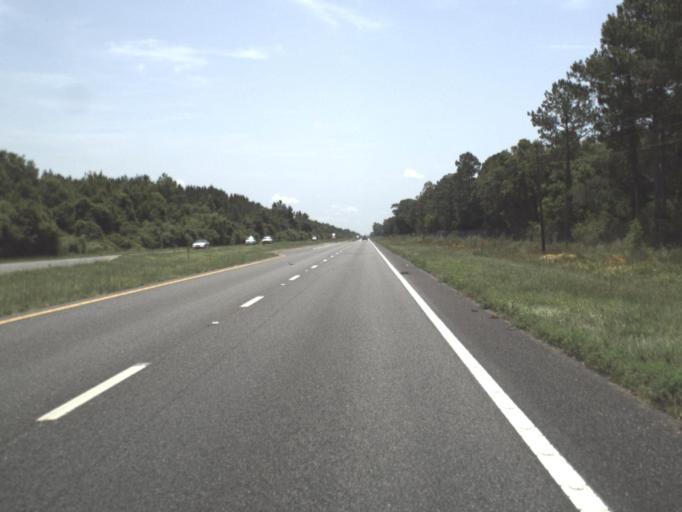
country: US
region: Florida
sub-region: Taylor County
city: Steinhatchee
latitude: 29.8664
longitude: -83.3946
